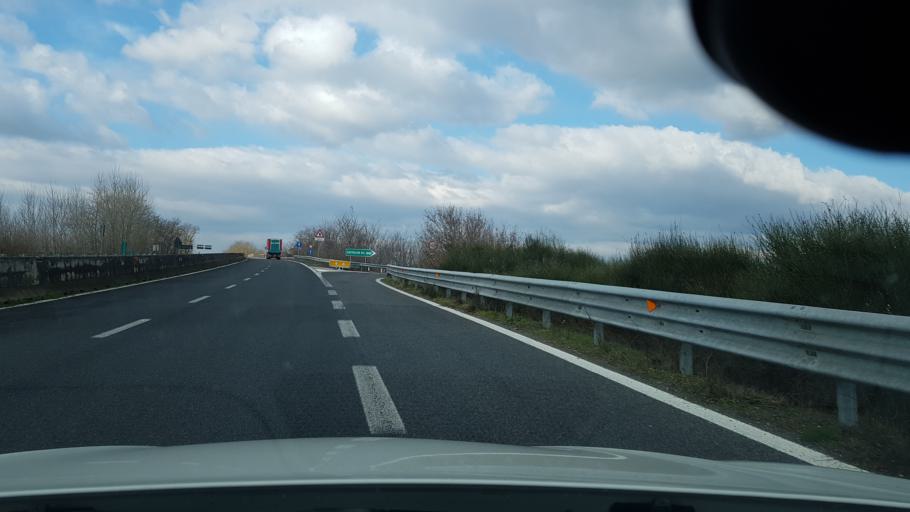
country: IT
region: Tuscany
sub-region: Province of Arezzo
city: Terontola
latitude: 43.1899
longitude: 12.0167
